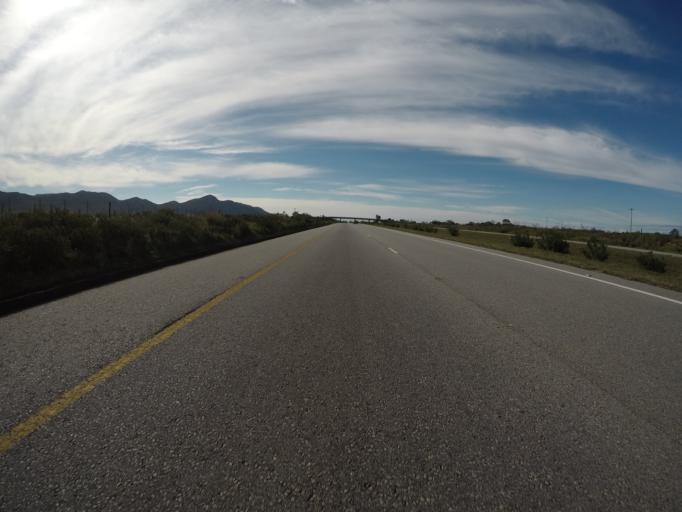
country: ZA
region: Eastern Cape
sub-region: Nelson Mandela Bay Metropolitan Municipality
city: Uitenhage
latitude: -33.9100
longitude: 25.2148
